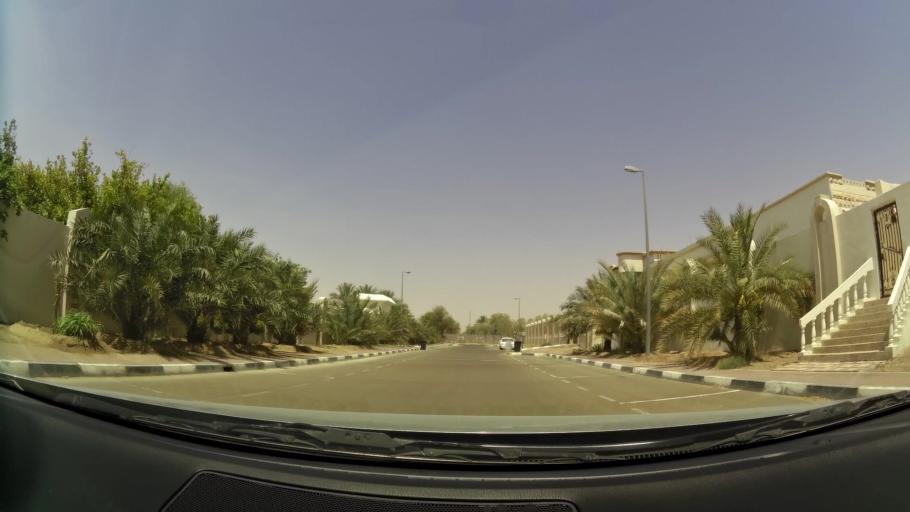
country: OM
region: Al Buraimi
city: Al Buraymi
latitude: 24.2866
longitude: 55.7559
